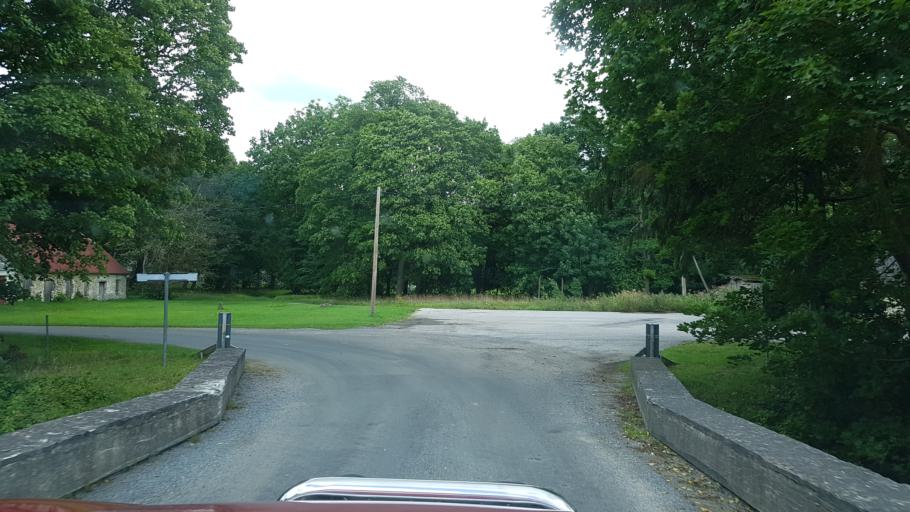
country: EE
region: Laeaene
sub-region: Lihula vald
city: Lihula
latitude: 58.7068
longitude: 24.0252
